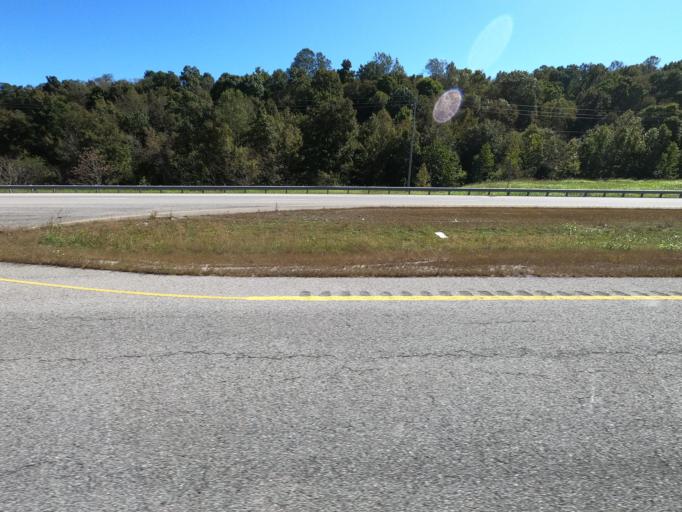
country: US
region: Tennessee
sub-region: Maury County
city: Mount Pleasant
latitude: 35.4770
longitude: -87.2608
